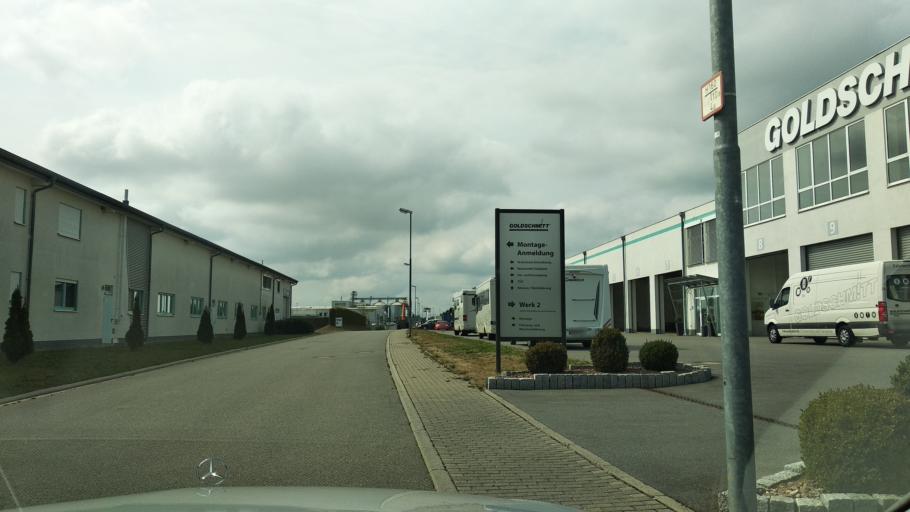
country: DE
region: Baden-Wuerttemberg
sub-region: Karlsruhe Region
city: Walldurn
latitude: 49.5895
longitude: 9.3934
